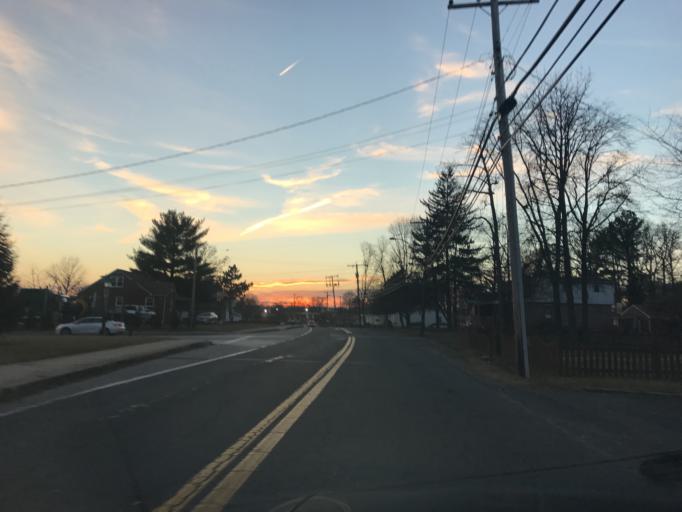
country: US
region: Maryland
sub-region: Baltimore County
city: Middle River
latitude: 39.3062
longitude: -76.4390
